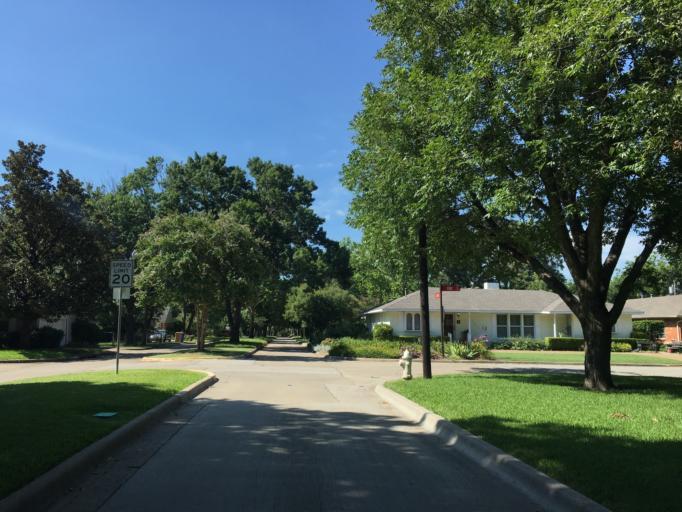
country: US
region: Texas
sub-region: Dallas County
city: Farmers Branch
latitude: 32.9221
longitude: -96.8769
